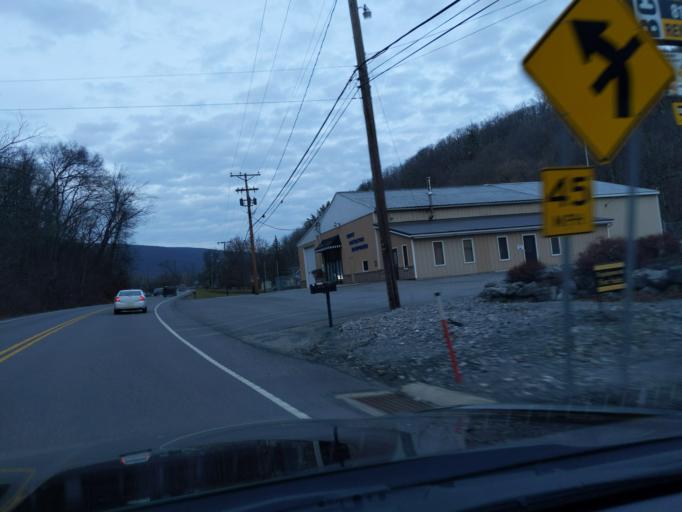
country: US
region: Pennsylvania
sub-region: Blair County
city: Hollidaysburg
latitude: 40.4492
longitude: -78.3531
